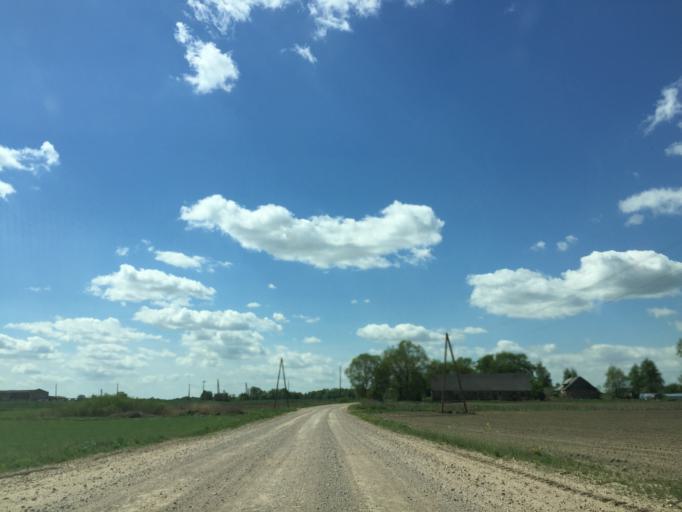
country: LV
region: Bauskas Rajons
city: Bauska
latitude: 56.4982
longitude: 24.1463
